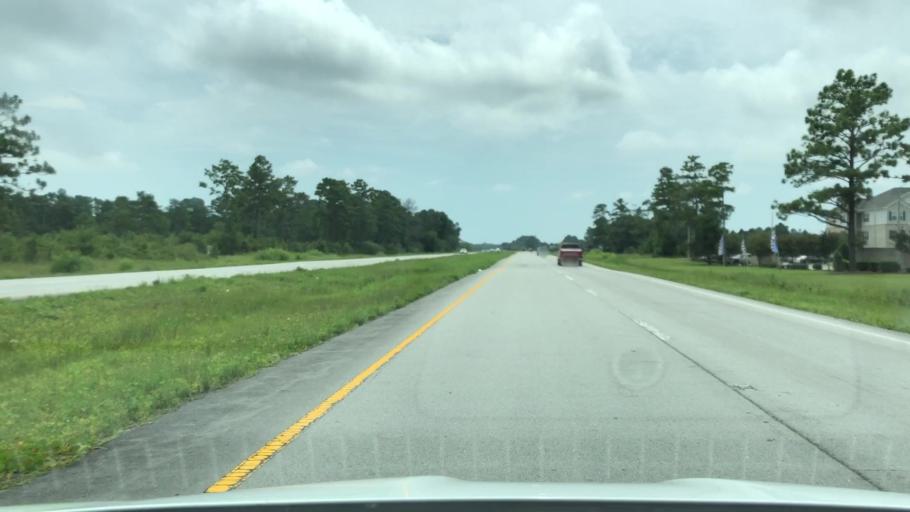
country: US
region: North Carolina
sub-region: Carteret County
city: Newport
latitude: 34.7972
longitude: -76.8779
